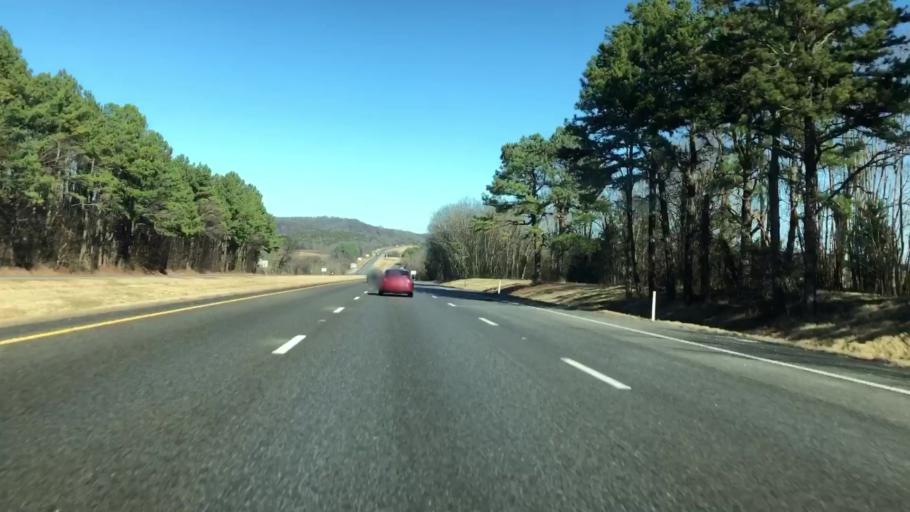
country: US
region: Tennessee
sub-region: Marshall County
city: Cornersville
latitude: 35.3115
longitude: -86.8821
